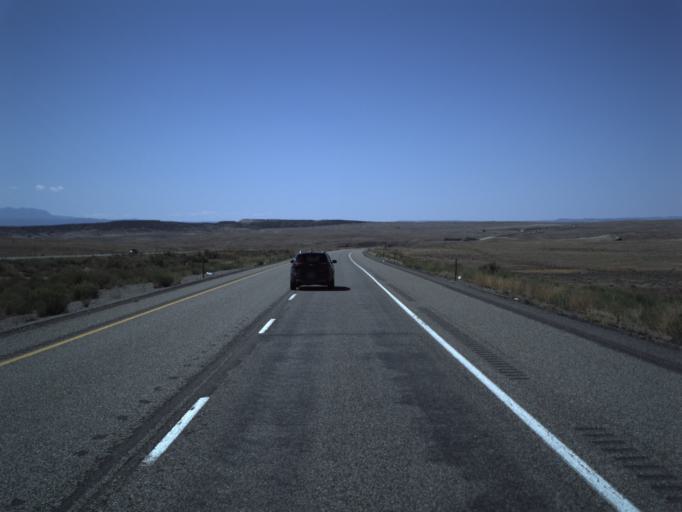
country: US
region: Colorado
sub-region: Mesa County
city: Loma
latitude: 39.1383
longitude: -109.1570
